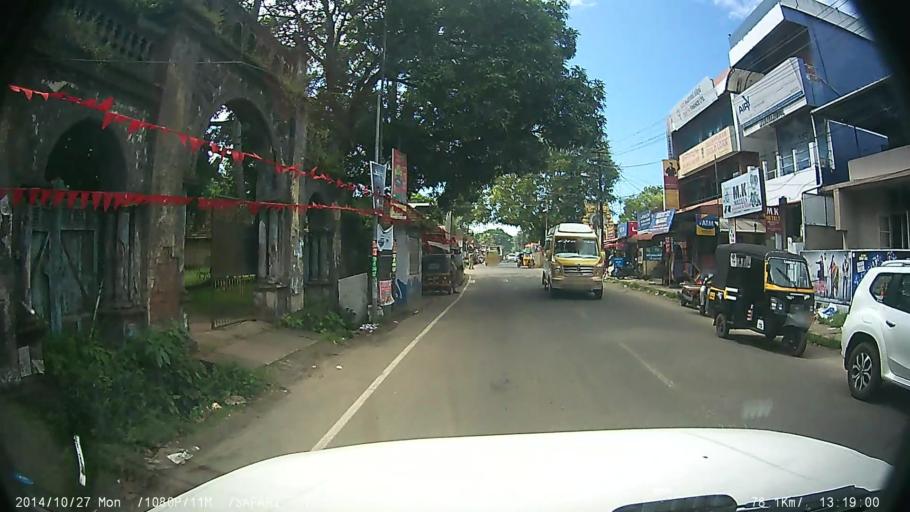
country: IN
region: Kerala
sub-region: Alappuzha
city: Alleppey
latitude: 9.4918
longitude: 76.3344
